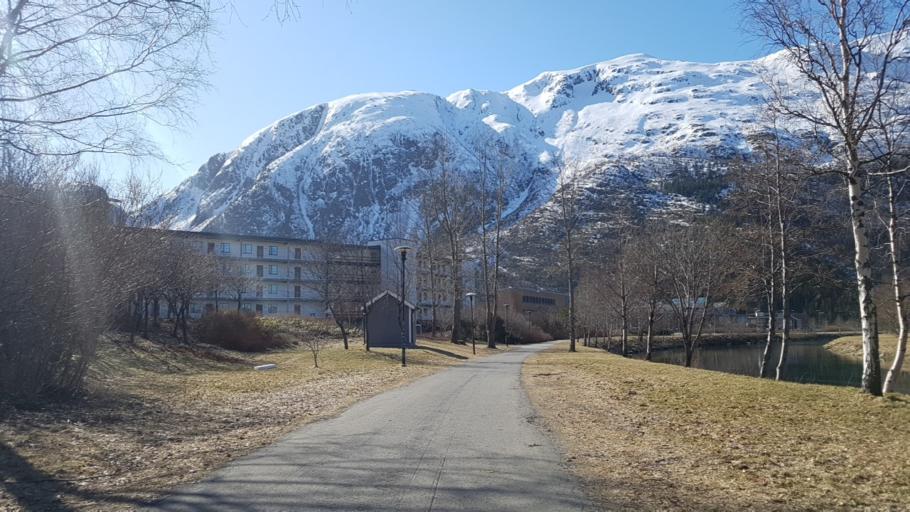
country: NO
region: Nordland
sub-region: Vefsn
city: Mosjoen
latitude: 65.8409
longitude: 13.1977
